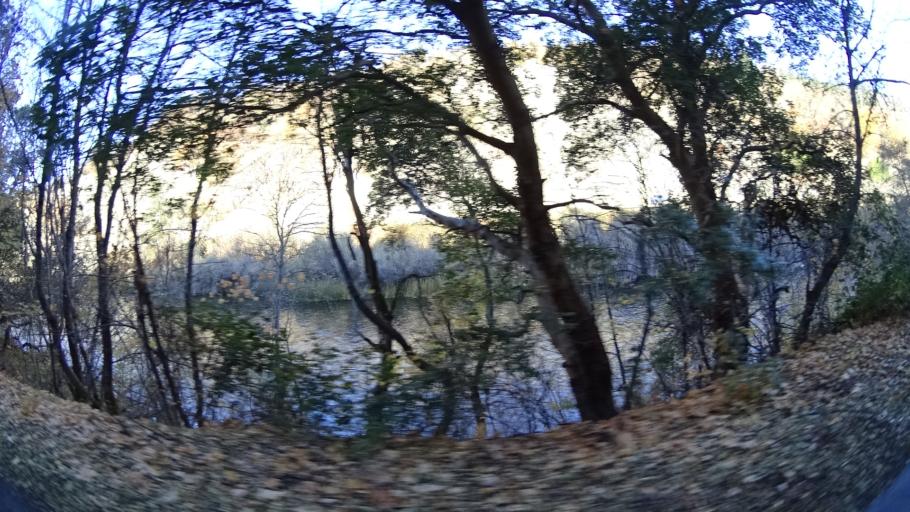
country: US
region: California
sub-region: Siskiyou County
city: Yreka
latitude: 41.8421
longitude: -122.9126
